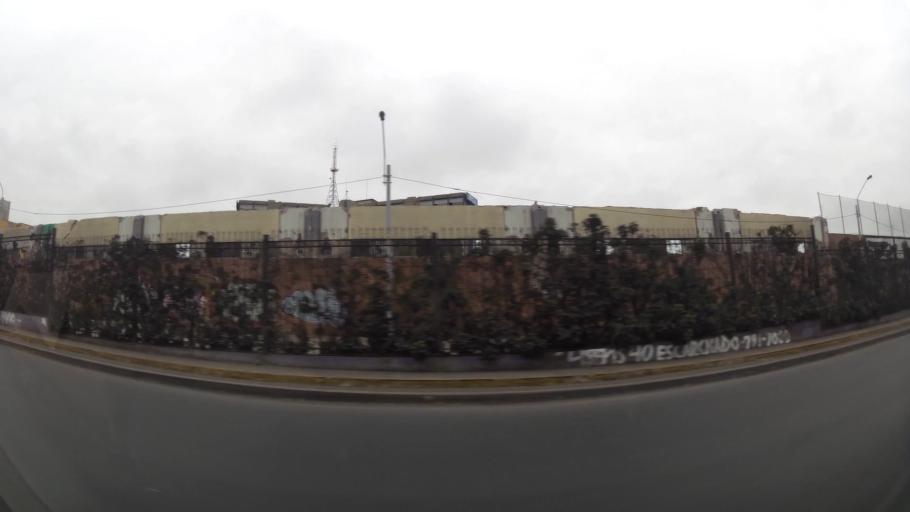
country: PE
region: Lima
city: Lima
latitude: -12.0478
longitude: -77.0564
